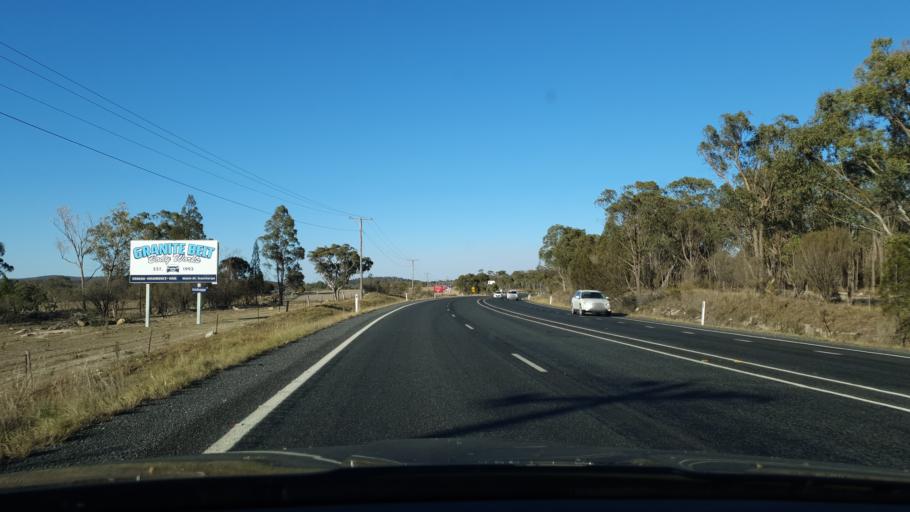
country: AU
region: Queensland
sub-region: Southern Downs
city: Stanthorpe
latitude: -28.6912
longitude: 151.9083
